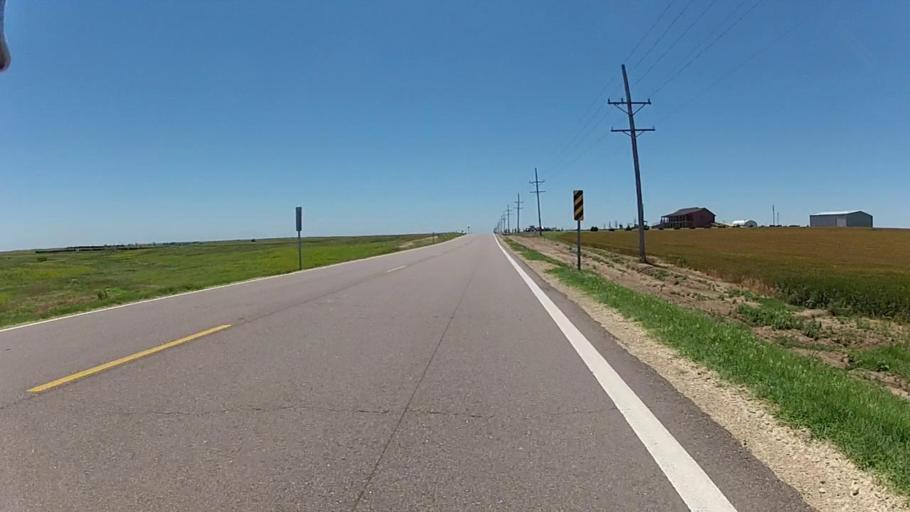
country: US
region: Kansas
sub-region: Kiowa County
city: Greensburg
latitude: 37.5045
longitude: -99.3204
